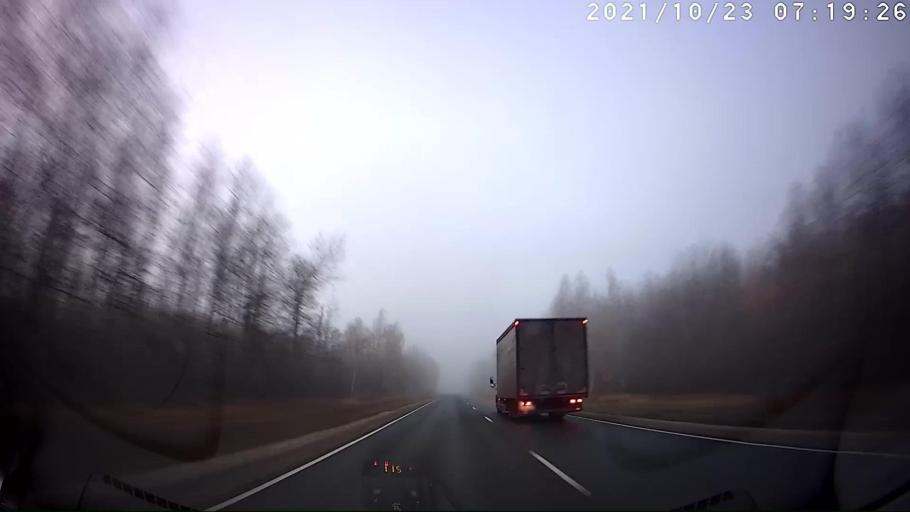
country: RU
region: Saratov
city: Khvalynsk
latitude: 52.4376
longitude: 48.0093
